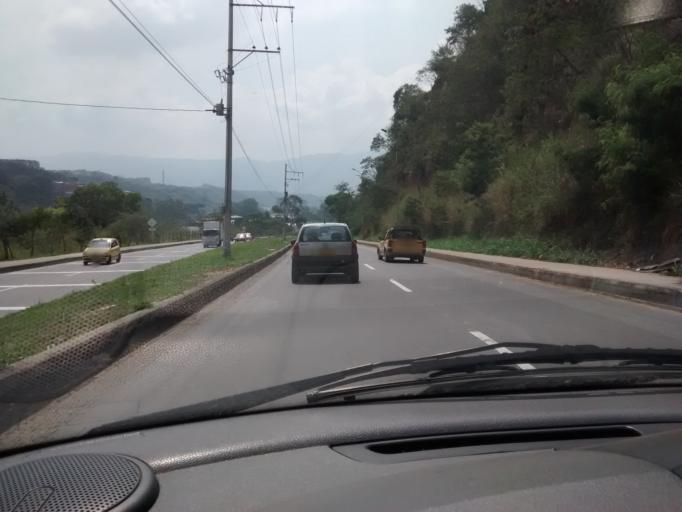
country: CO
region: Santander
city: Bucaramanga
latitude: 7.0936
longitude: -73.1211
